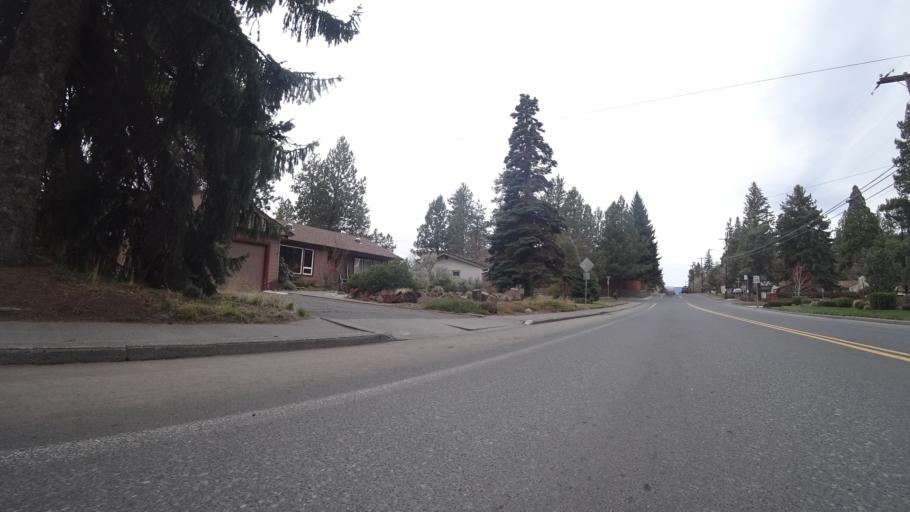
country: US
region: Oregon
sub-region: Deschutes County
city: Bend
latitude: 44.0559
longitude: -121.2947
